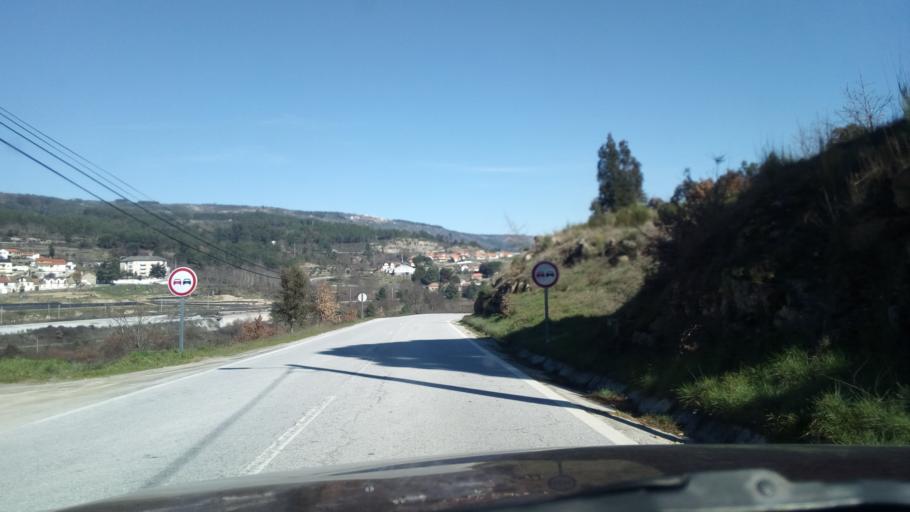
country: PT
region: Guarda
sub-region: Fornos de Algodres
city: Fornos de Algodres
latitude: 40.6079
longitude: -7.5242
